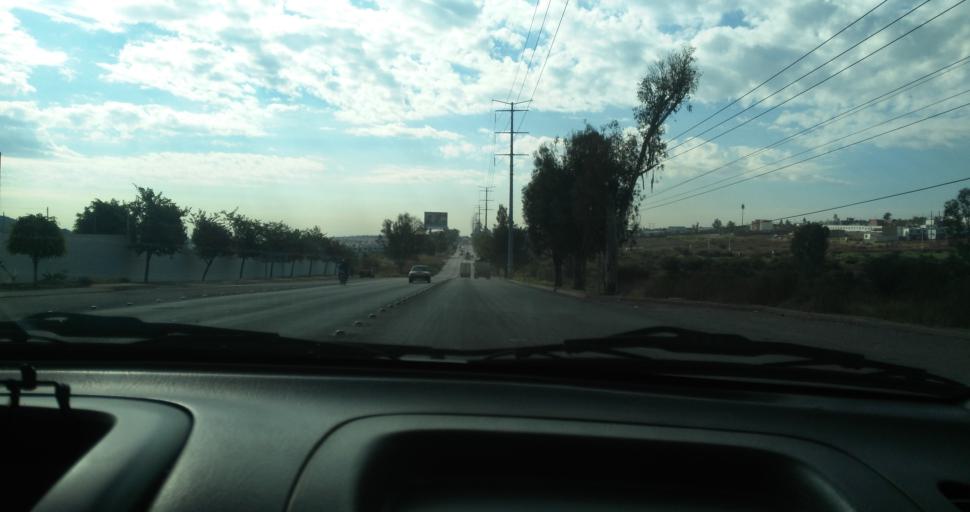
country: MX
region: Guanajuato
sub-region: Leon
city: Fraccionamiento Paseo de las Torres
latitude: 21.1746
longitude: -101.7396
